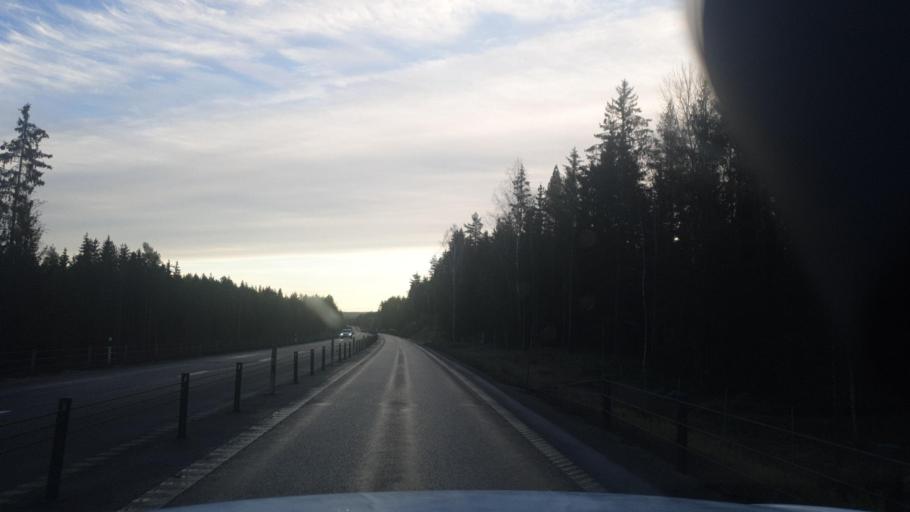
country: SE
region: Vaermland
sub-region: Arvika Kommun
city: Arvika
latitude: 59.6454
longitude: 12.7015
